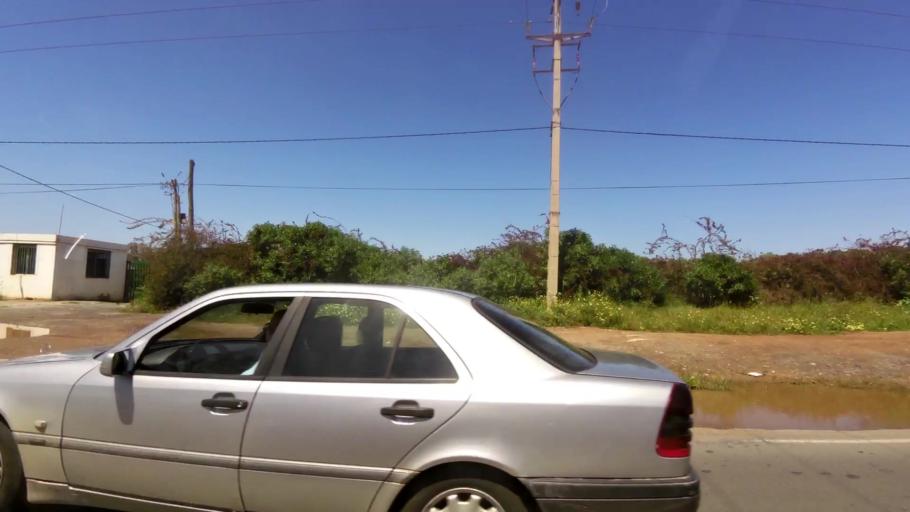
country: MA
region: Grand Casablanca
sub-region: Nouaceur
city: Dar Bouazza
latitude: 33.5255
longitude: -7.7818
